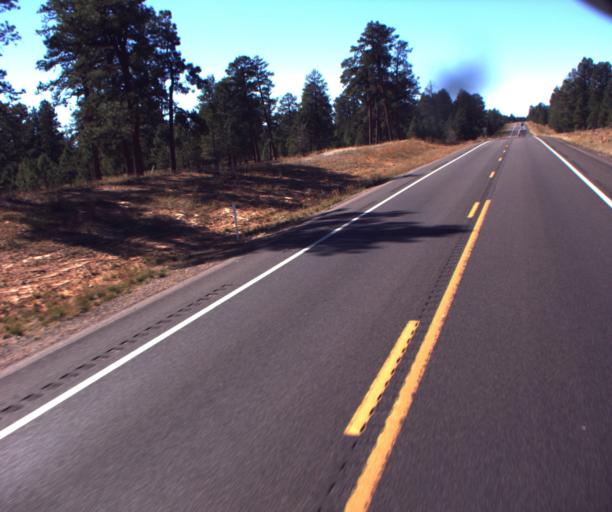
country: US
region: Arizona
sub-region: Apache County
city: Saint Michaels
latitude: 35.6829
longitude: -109.2249
